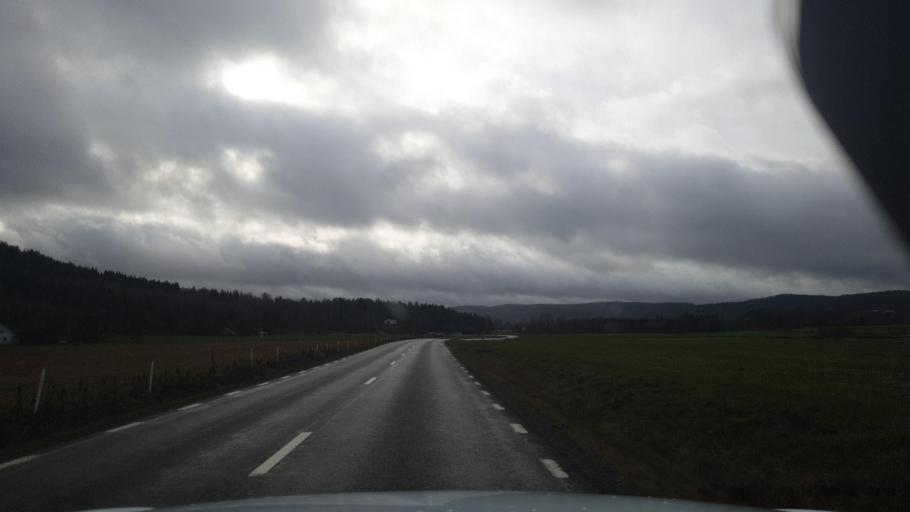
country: SE
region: Vaermland
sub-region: Eda Kommun
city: Amotfors
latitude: 59.6497
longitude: 12.1402
